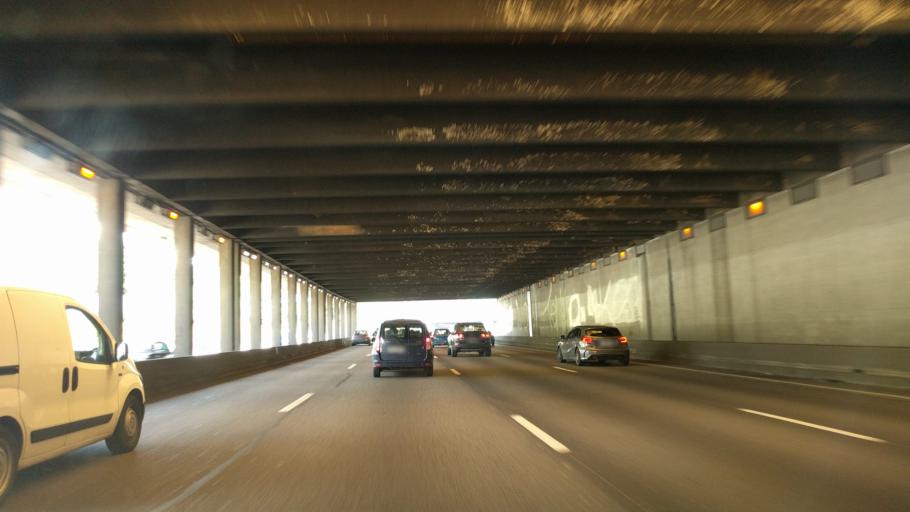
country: FR
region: Ile-de-France
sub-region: Departement des Hauts-de-Seine
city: Levallois-Perret
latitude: 48.8872
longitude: 2.2906
